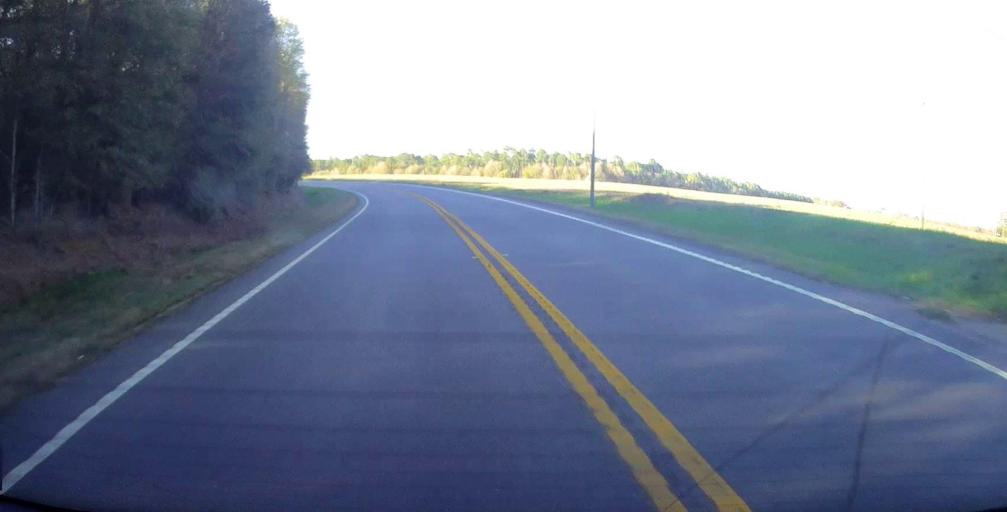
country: US
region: Georgia
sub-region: Pulaski County
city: Hawkinsville
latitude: 32.2514
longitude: -83.4103
